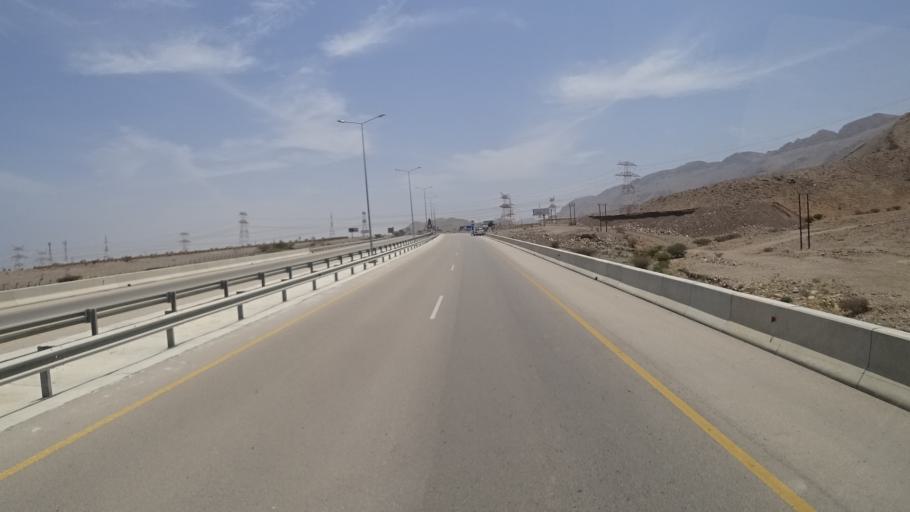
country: OM
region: Ash Sharqiyah
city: Sur
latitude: 22.6542
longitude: 59.3929
